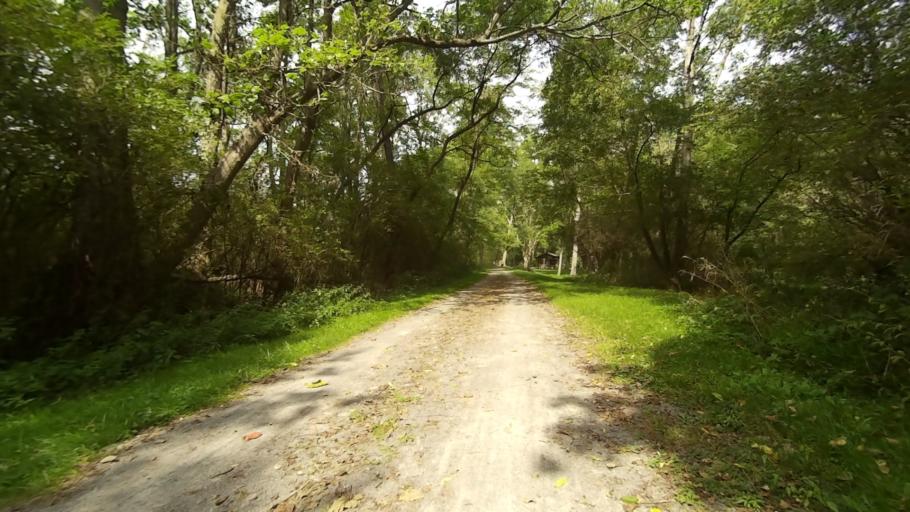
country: US
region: Pennsylvania
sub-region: Blair County
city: Williamsburg
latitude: 40.5199
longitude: -78.1710
